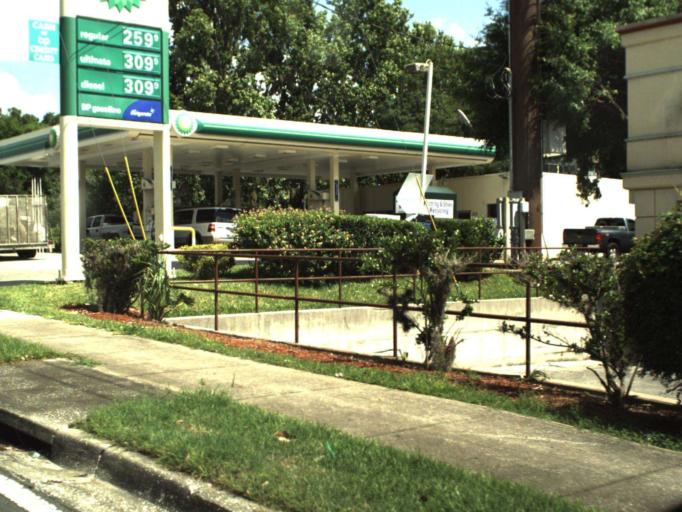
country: US
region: Florida
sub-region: Marion County
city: Ocala
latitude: 29.1715
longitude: -82.1276
